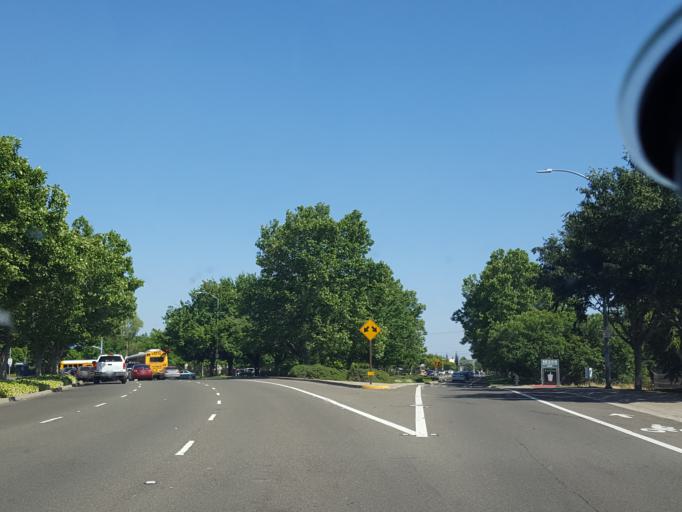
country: US
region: California
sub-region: Sacramento County
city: Rancho Cordova
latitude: 38.5739
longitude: -121.3025
